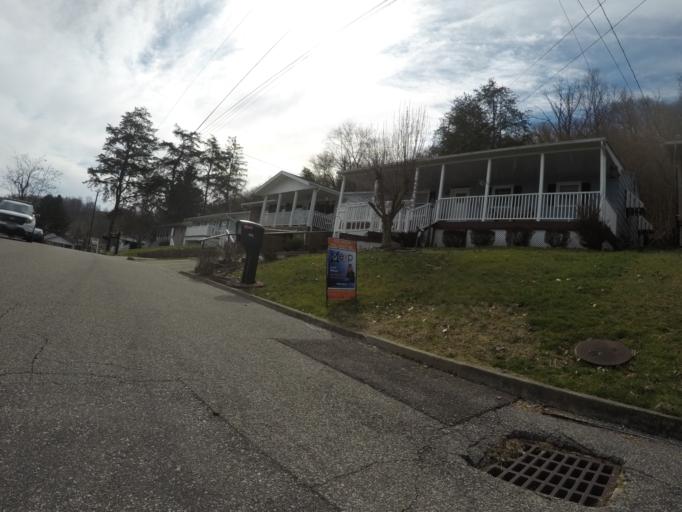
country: US
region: West Virginia
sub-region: Cabell County
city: Barboursville
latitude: 38.4021
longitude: -82.2988
